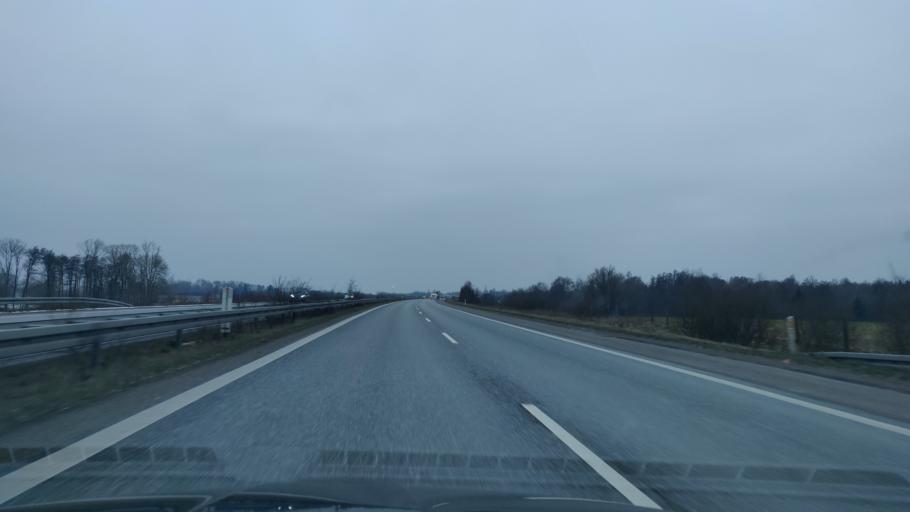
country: DK
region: South Denmark
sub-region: Faaborg-Midtfyn Kommune
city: Arslev
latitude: 55.2898
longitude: 10.4438
